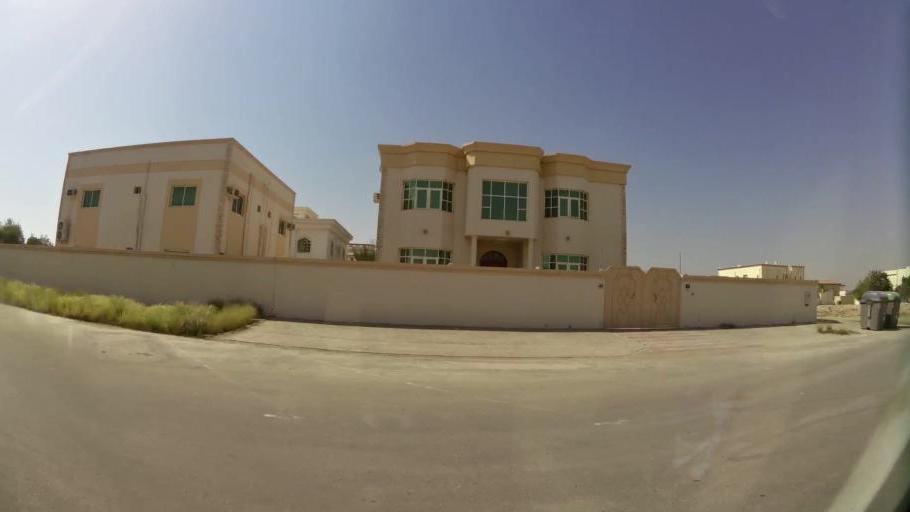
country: AE
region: Ajman
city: Ajman
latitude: 25.4158
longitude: 55.4703
